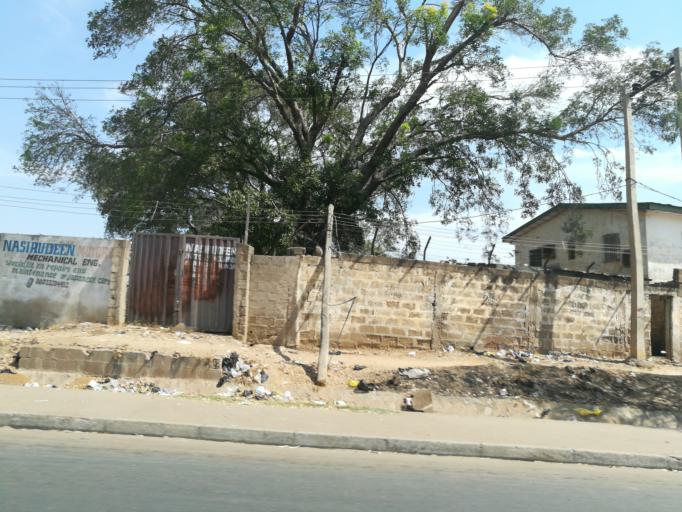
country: NG
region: Kano
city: Kano
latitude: 12.0228
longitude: 8.5163
